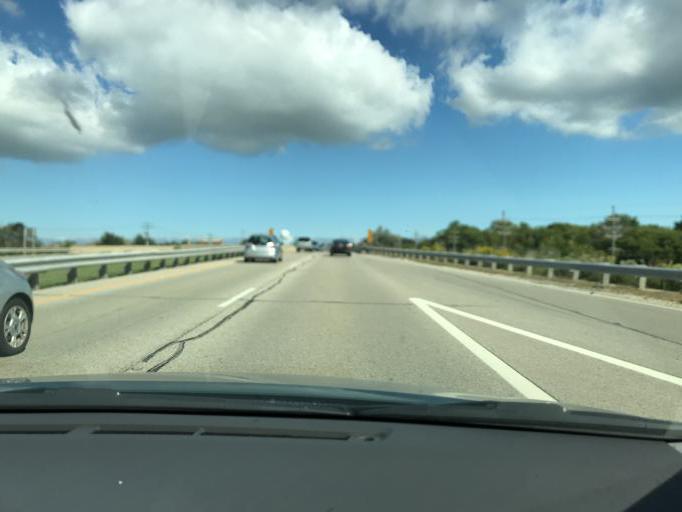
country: US
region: Wisconsin
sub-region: Kenosha County
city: Pleasant Prairie
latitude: 42.5667
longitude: -87.8994
